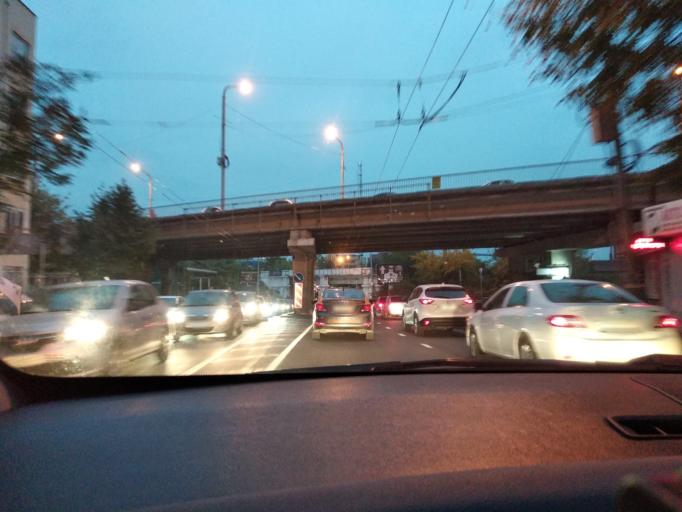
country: RU
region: Krasnodarskiy
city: Krasnodar
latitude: 45.0136
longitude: 38.9750
